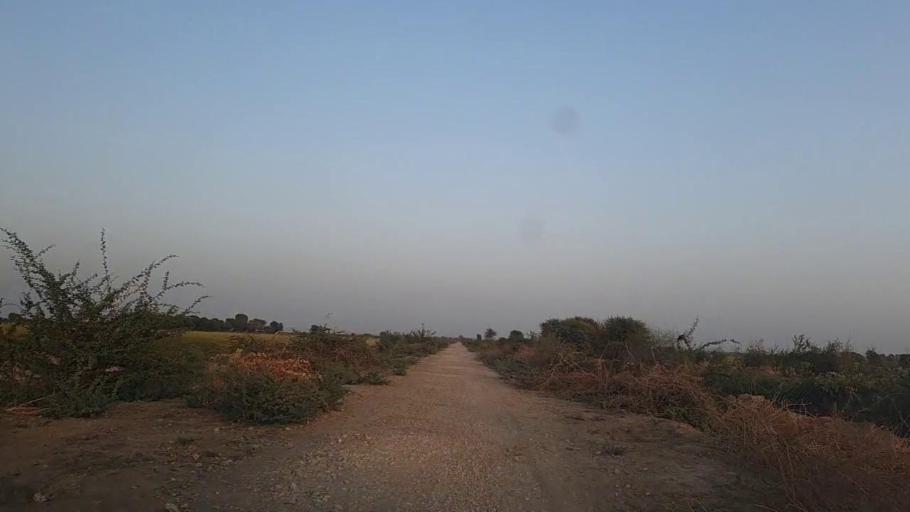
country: PK
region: Sindh
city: Naukot
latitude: 24.6958
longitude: 69.2744
